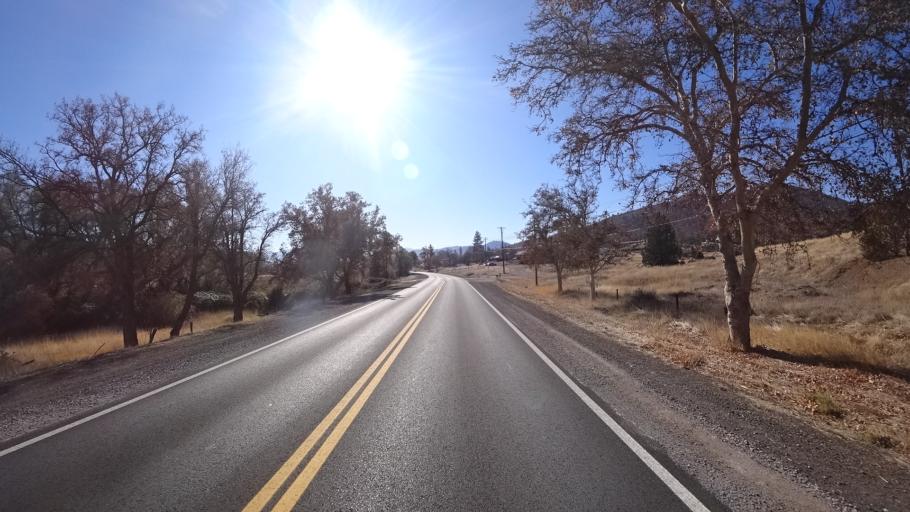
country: US
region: California
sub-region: Siskiyou County
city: Yreka
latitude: 41.7579
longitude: -122.6251
